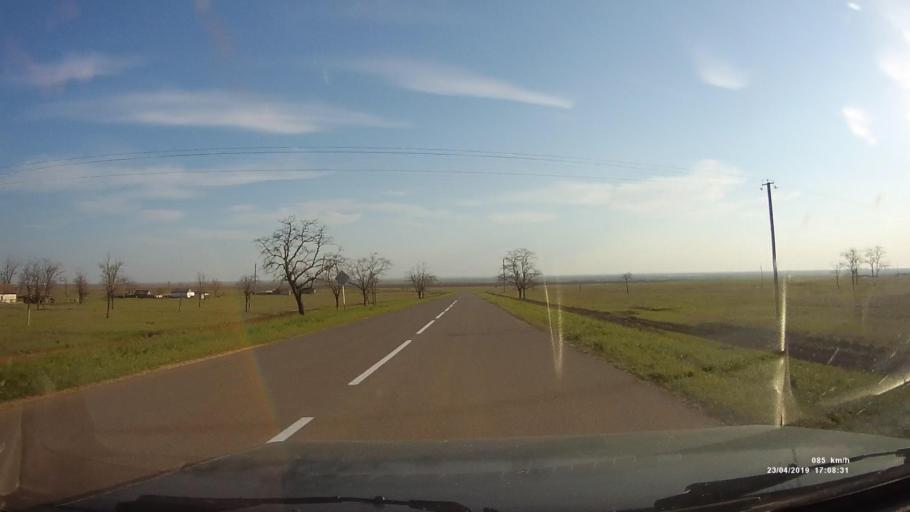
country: RU
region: Kalmykiya
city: Priyutnoye
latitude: 46.2703
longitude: 43.4871
